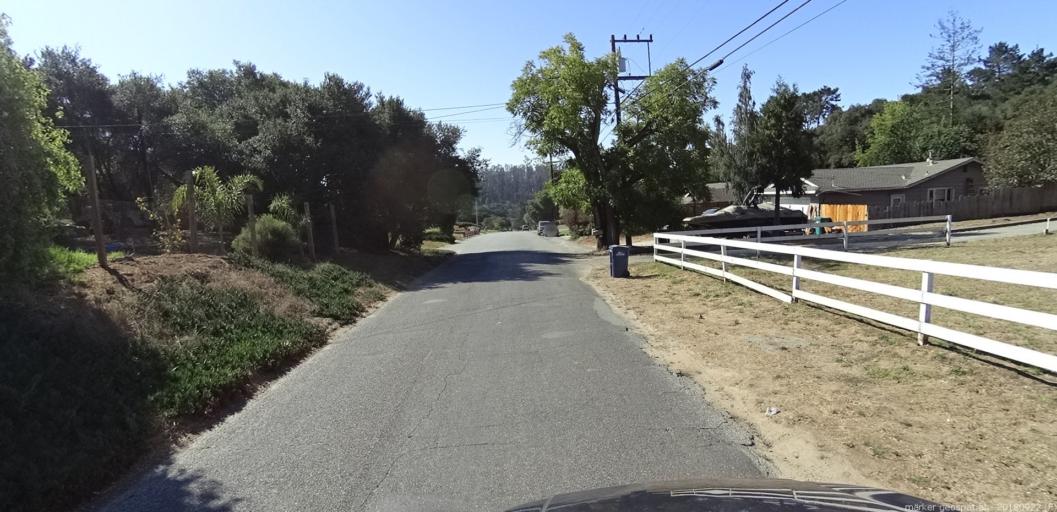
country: US
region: California
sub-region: Monterey County
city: Prunedale
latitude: 36.8160
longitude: -121.6547
